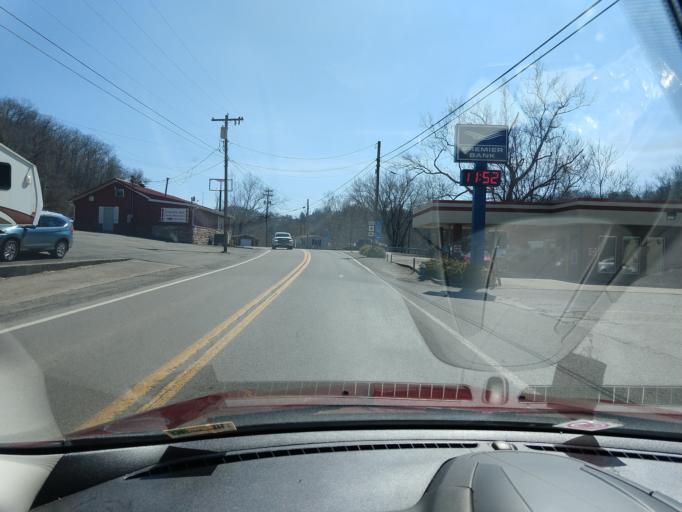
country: US
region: West Virginia
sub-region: Braxton County
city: Sutton
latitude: 38.6678
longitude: -80.7176
